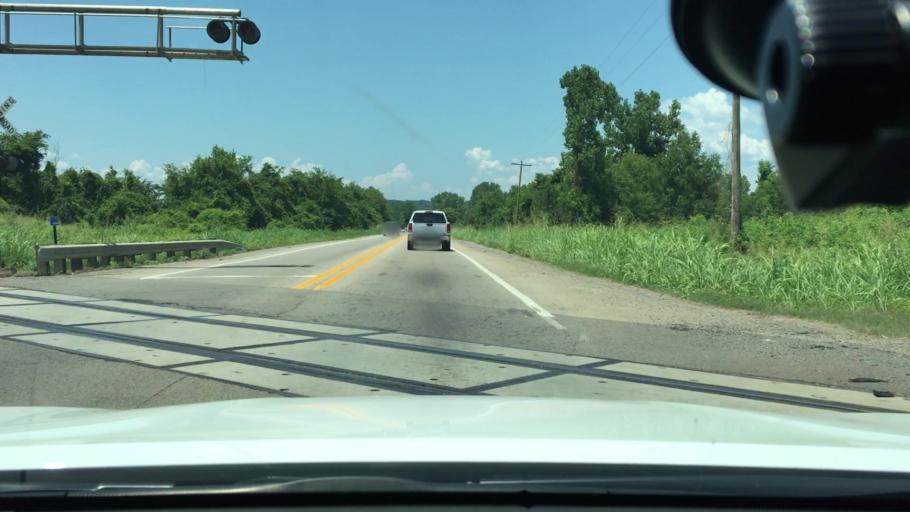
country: US
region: Arkansas
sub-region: Crawford County
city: Van Buren
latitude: 35.4185
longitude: -94.3350
